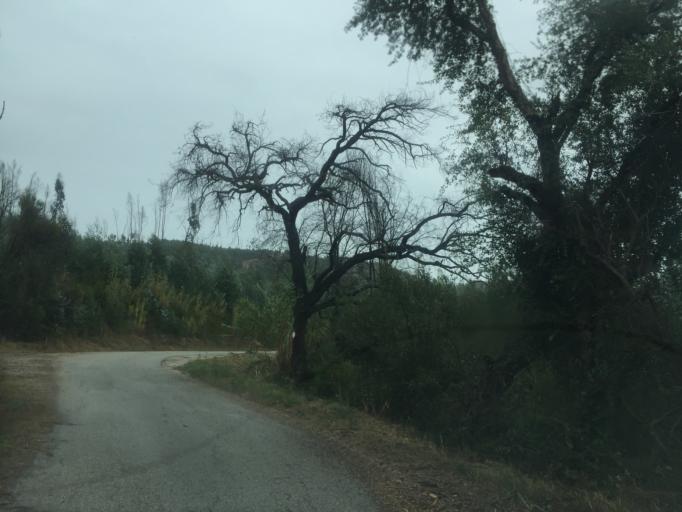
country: PT
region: Coimbra
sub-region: Figueira da Foz
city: Lavos
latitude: 40.0844
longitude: -8.8011
